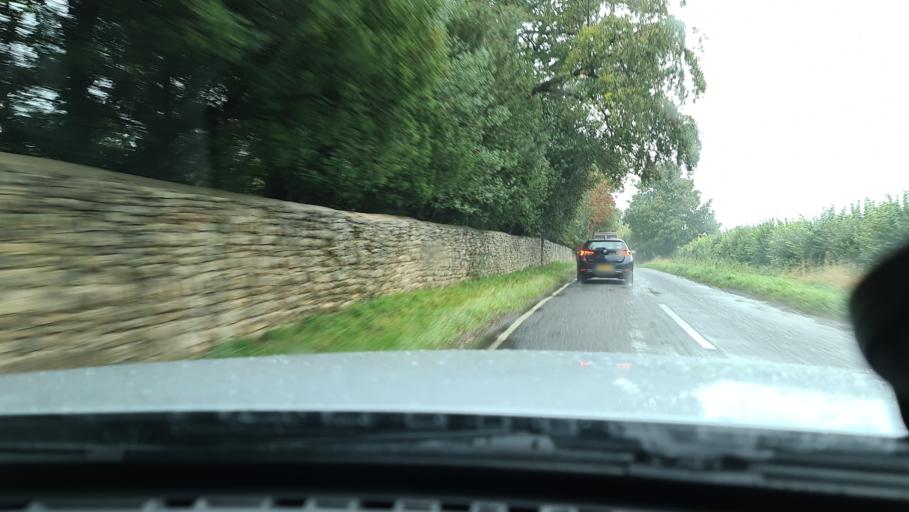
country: GB
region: England
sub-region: Oxfordshire
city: Woodstock
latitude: 51.8786
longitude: -1.3608
